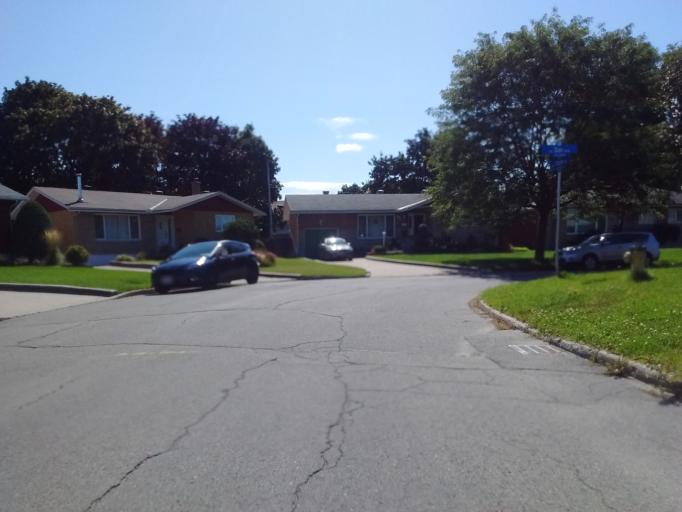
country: CA
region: Ontario
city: Ottawa
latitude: 45.4325
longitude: -75.6373
